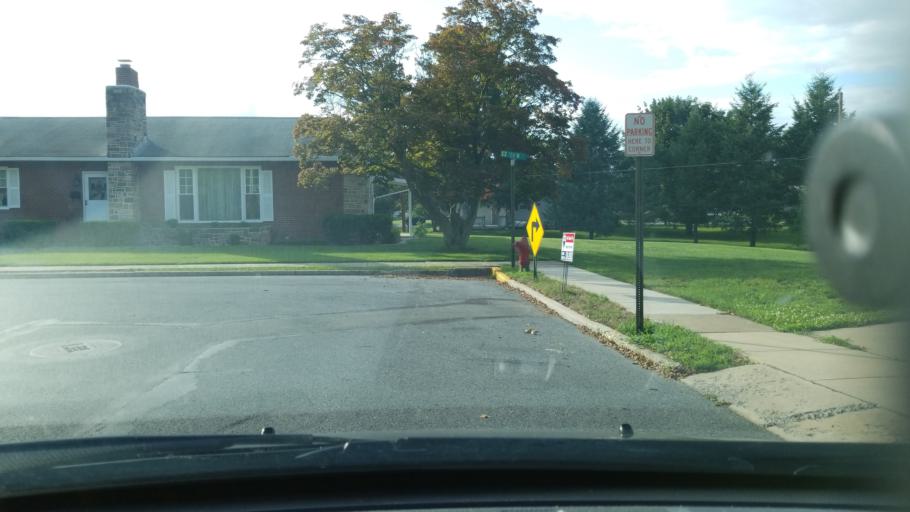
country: US
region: Pennsylvania
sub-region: Northumberland County
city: Watsontown
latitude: 41.0901
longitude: -76.8675
